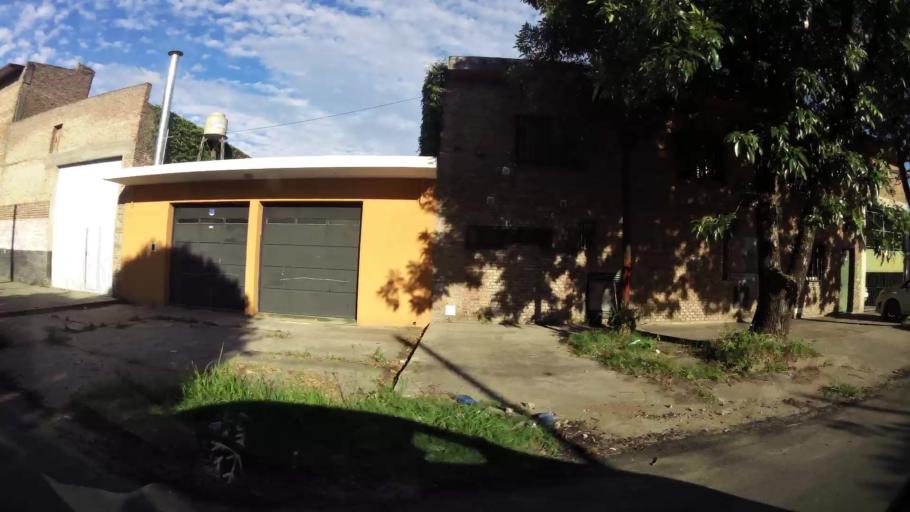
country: AR
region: Santa Fe
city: Gobernador Galvez
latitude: -32.9885
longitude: -60.6702
